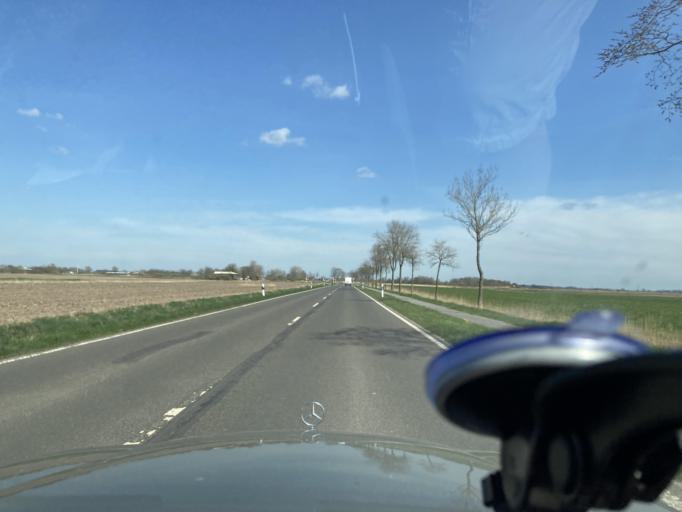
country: DE
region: Schleswig-Holstein
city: Lehe
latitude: 54.3443
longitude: 9.0362
